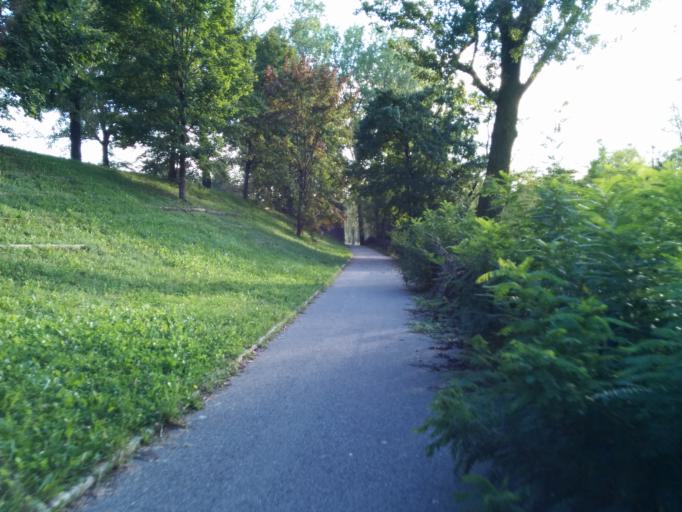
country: IT
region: Friuli Venezia Giulia
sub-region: Provincia di Udine
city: Colugna
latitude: 46.0860
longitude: 13.1888
